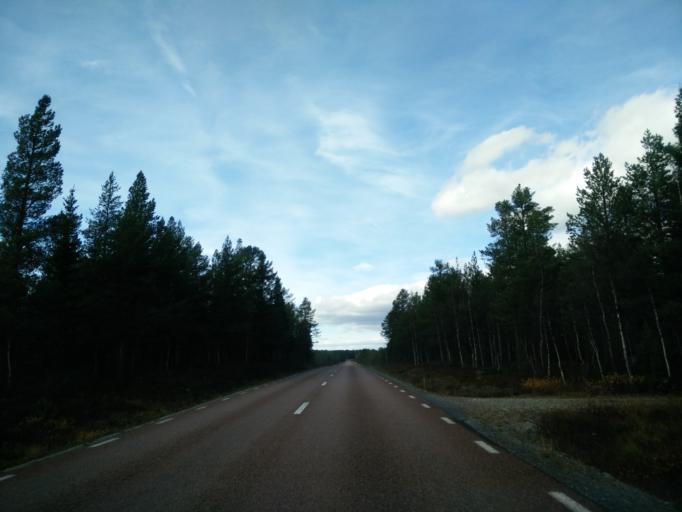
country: NO
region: Hedmark
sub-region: Engerdal
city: Engerdal
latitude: 62.4865
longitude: 12.6517
